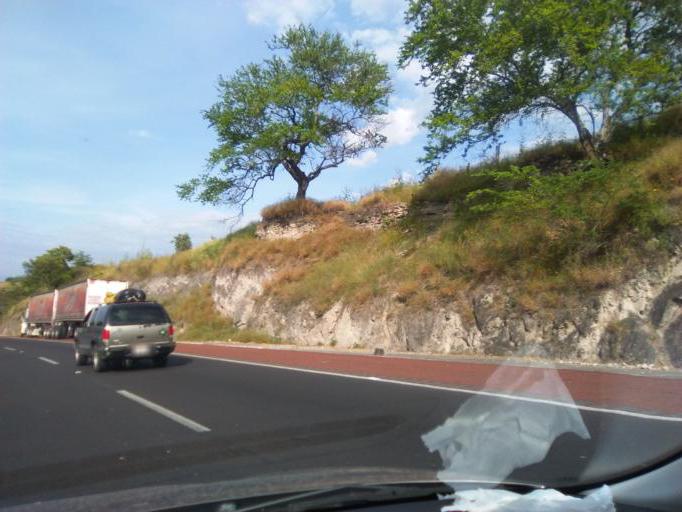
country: MX
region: Morelos
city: Alpuyeca
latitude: 18.7262
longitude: -99.2563
